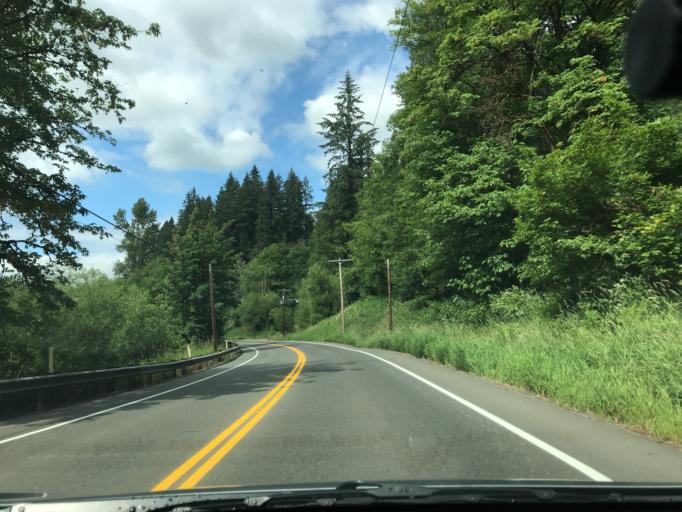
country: US
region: Washington
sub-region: King County
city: Lea Hill
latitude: 47.3035
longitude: -122.1717
